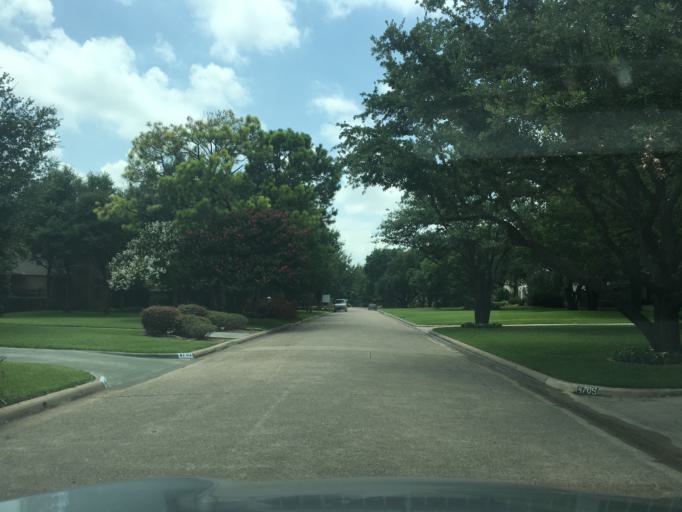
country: US
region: Texas
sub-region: Dallas County
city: University Park
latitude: 32.8986
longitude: -96.8272
